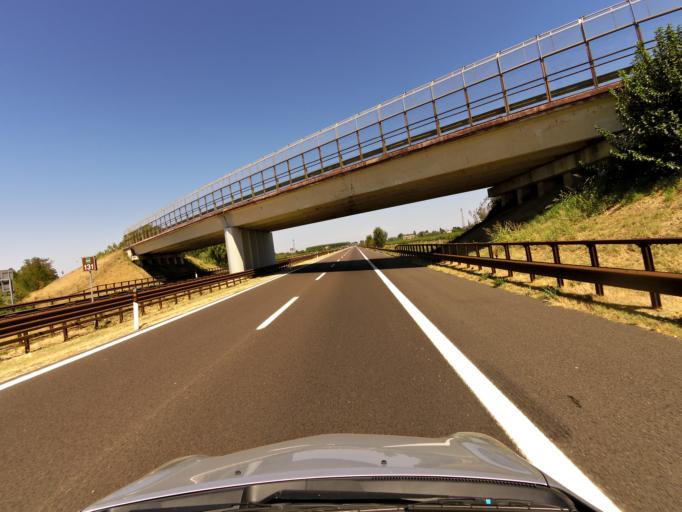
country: IT
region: Emilia-Romagna
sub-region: Provincia di Modena
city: Migliarina
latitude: 44.8019
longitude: 10.8520
